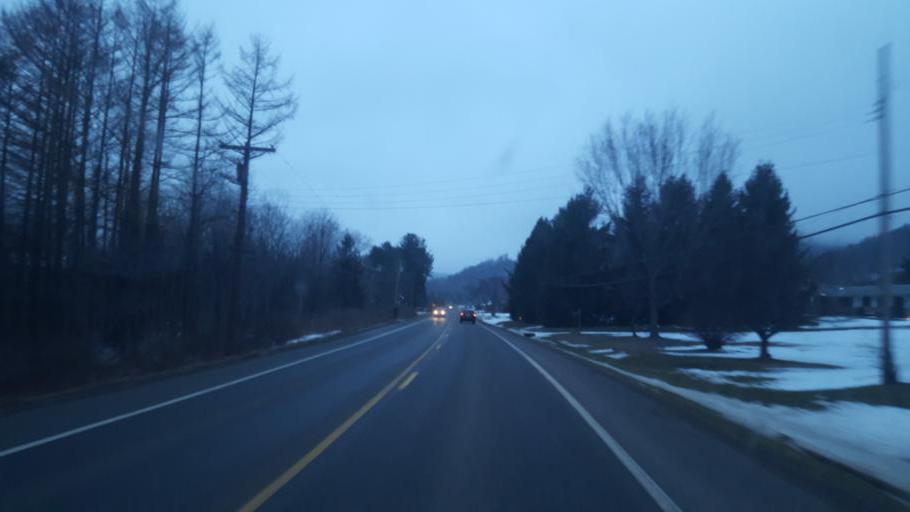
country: US
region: Pennsylvania
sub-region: Potter County
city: Coudersport
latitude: 41.7585
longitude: -78.1111
